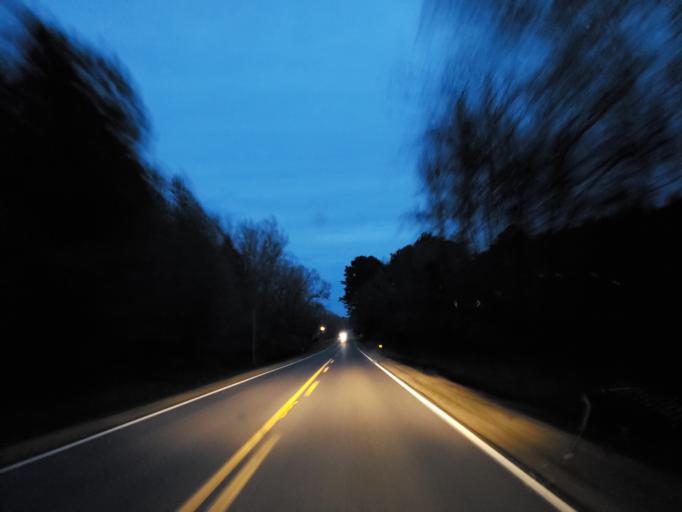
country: US
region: Alabama
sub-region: Greene County
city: Eutaw
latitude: 32.8838
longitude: -87.9386
